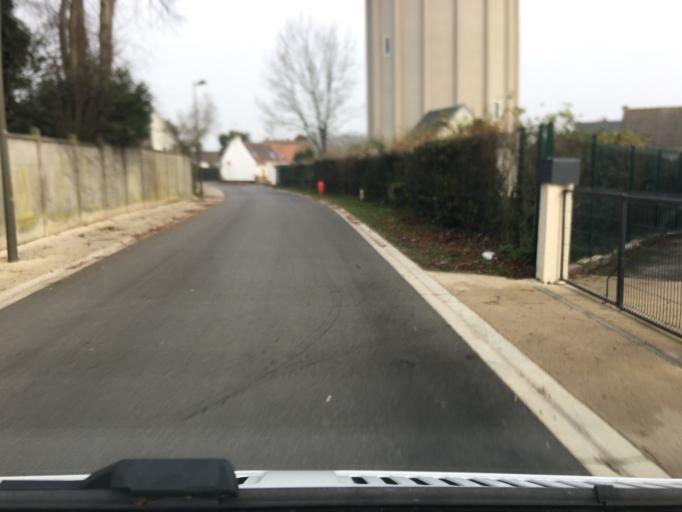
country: FR
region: Picardie
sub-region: Departement de la Somme
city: Saint-Valery-sur-Somme
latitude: 50.1800
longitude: 1.6317
